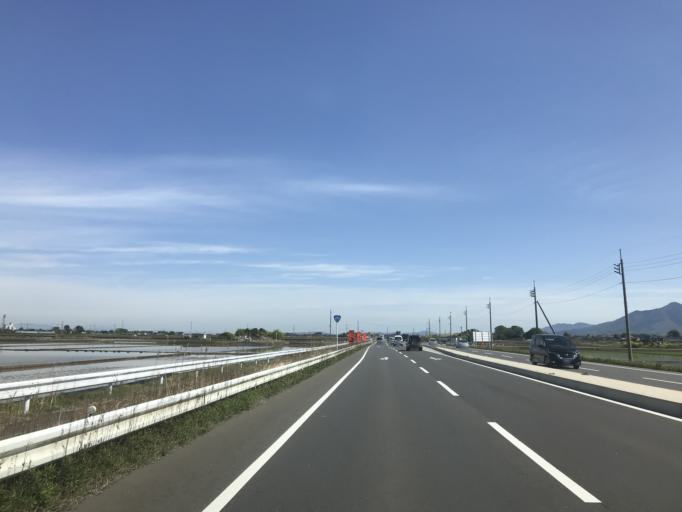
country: JP
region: Ibaraki
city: Ishige
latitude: 36.1391
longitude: 139.9868
